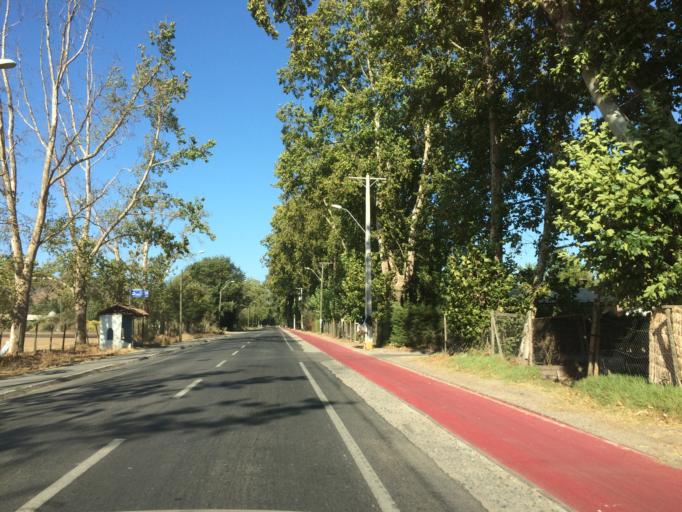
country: CL
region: Santiago Metropolitan
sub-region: Provincia de Melipilla
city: Melipilla
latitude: -33.4903
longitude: -71.1895
